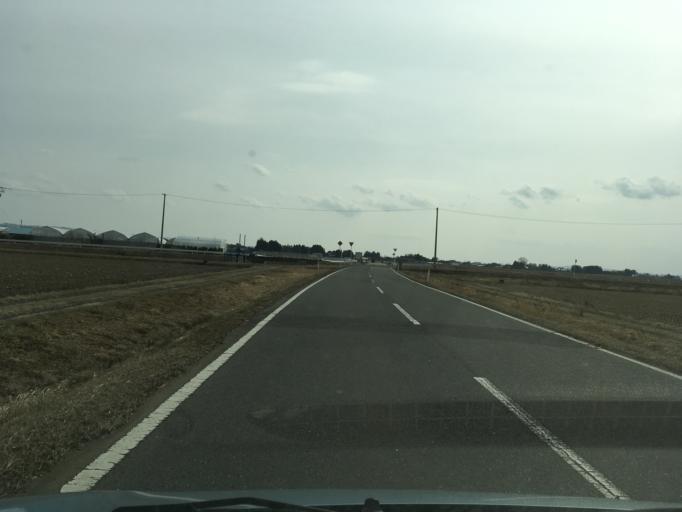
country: JP
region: Miyagi
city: Wakuya
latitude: 38.7295
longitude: 141.2396
